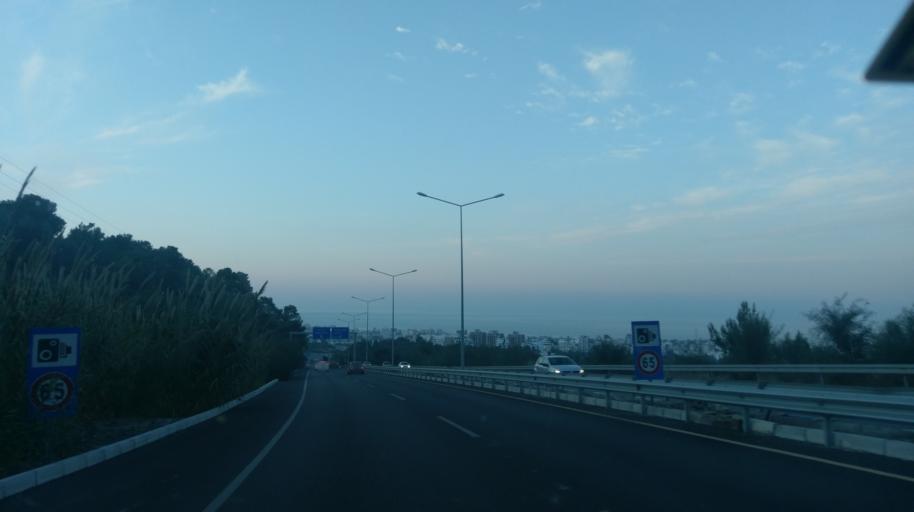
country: CY
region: Keryneia
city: Kyrenia
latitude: 35.3192
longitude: 33.3213
